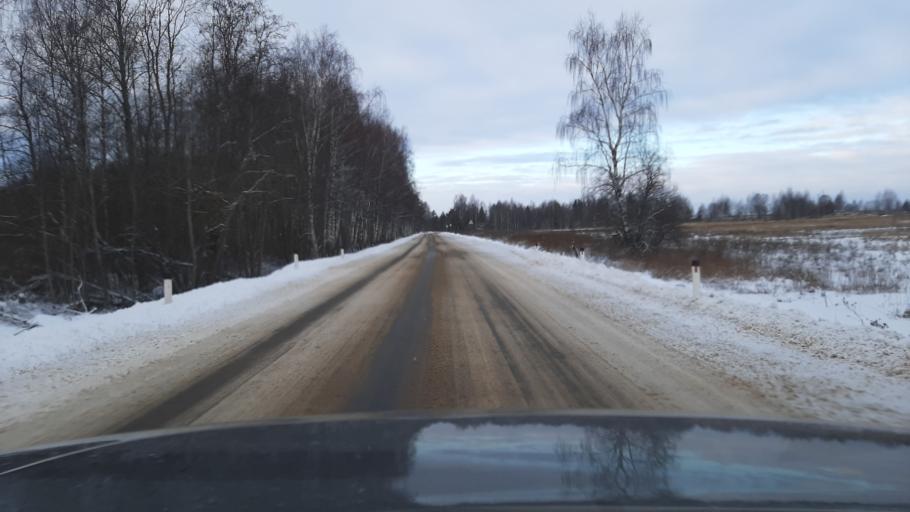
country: RU
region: Kostroma
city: Nerekhta
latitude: 57.4720
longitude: 40.6479
